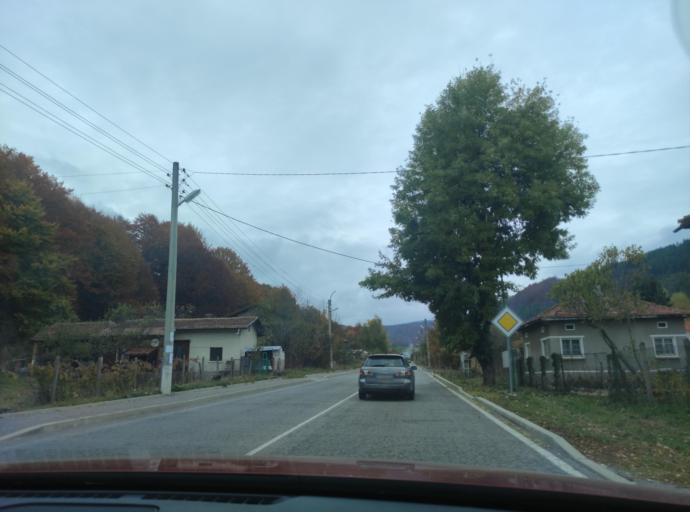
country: BG
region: Sofiya
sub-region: Obshtina Godech
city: Godech
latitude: 43.0822
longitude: 23.1040
